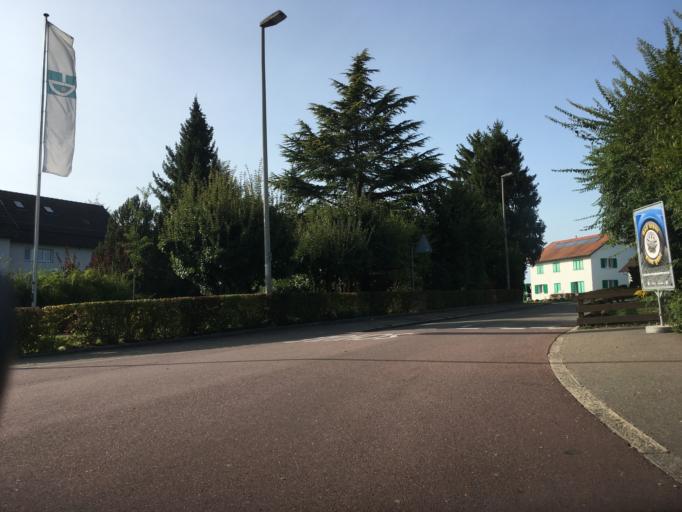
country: CH
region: Zurich
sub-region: Bezirk Buelach
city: Wallisellen / Rieden
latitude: 47.4156
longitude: 8.6019
